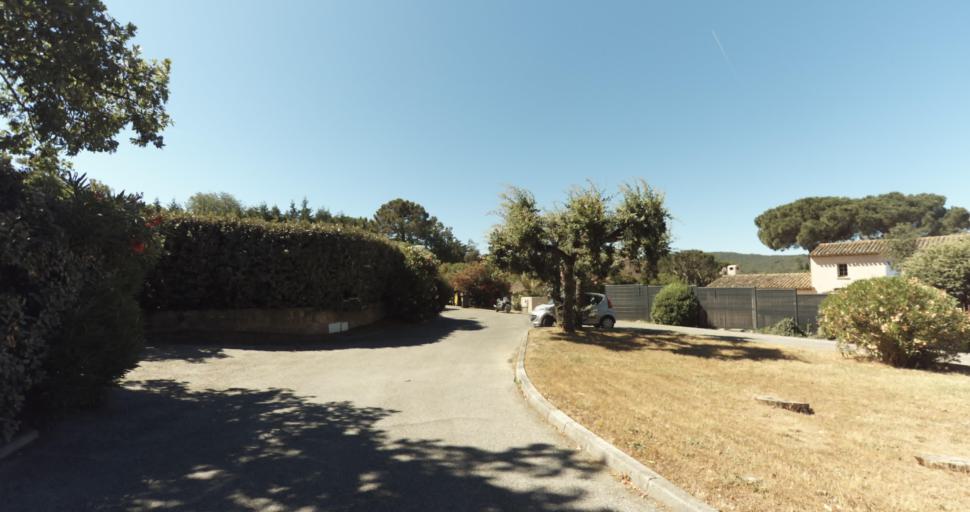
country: FR
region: Provence-Alpes-Cote d'Azur
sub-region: Departement du Var
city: Gassin
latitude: 43.2583
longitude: 6.5995
